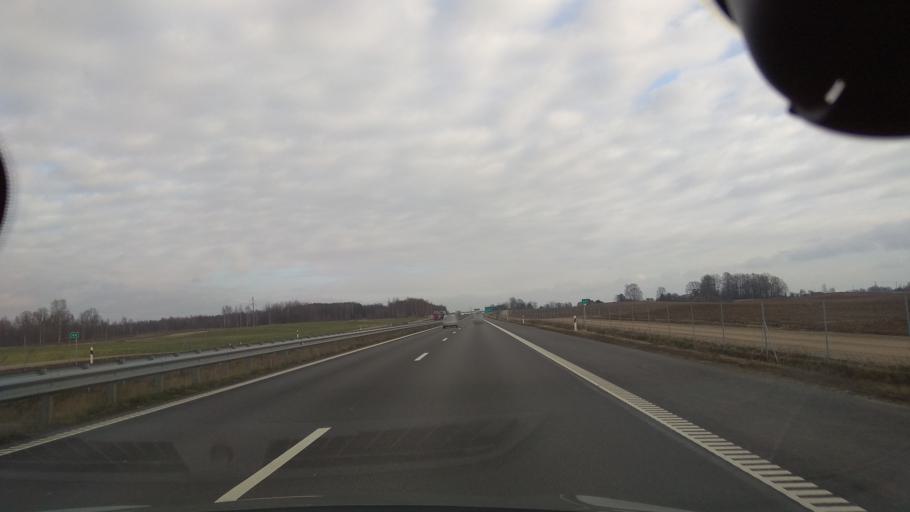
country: LT
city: Ezerelis
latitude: 54.7195
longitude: 23.6681
